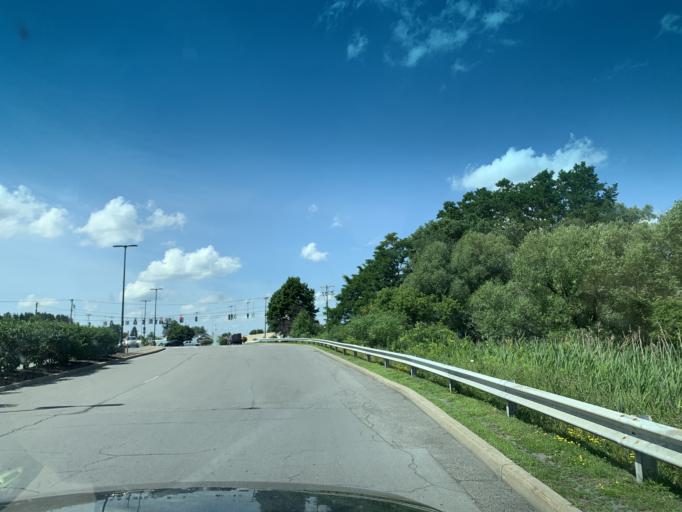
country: US
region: New York
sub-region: Oneida County
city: New Hartford
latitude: 43.0853
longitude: -75.3145
